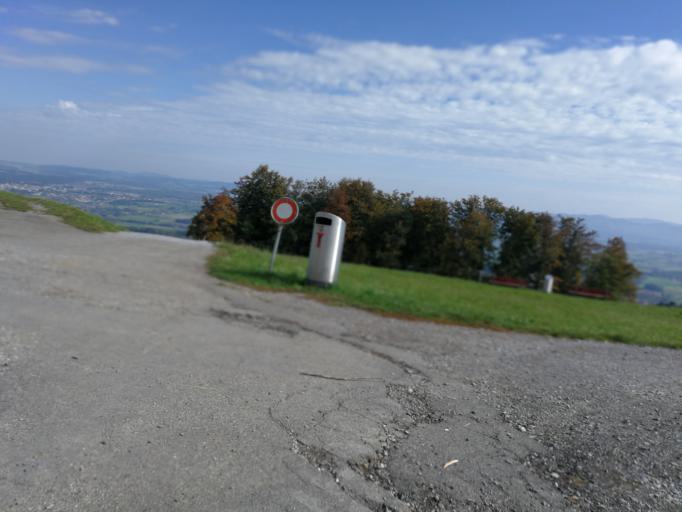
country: CH
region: Zurich
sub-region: Bezirk Uster
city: Egg
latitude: 47.2898
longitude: 8.6758
